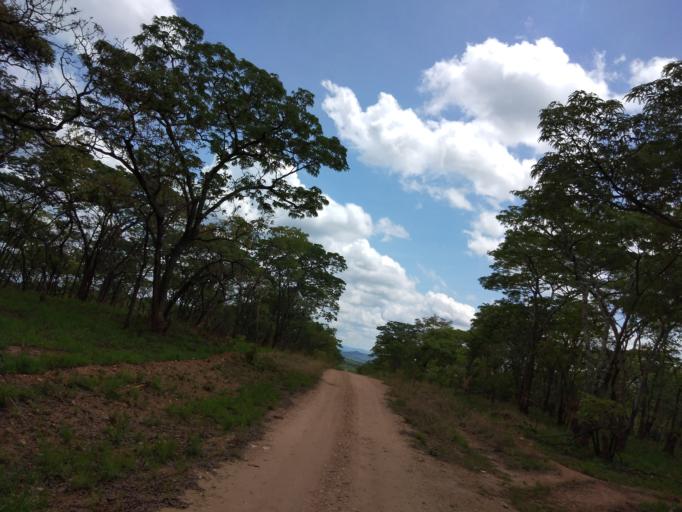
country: ZM
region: Central
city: Mkushi
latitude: -14.0545
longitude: 29.9612
